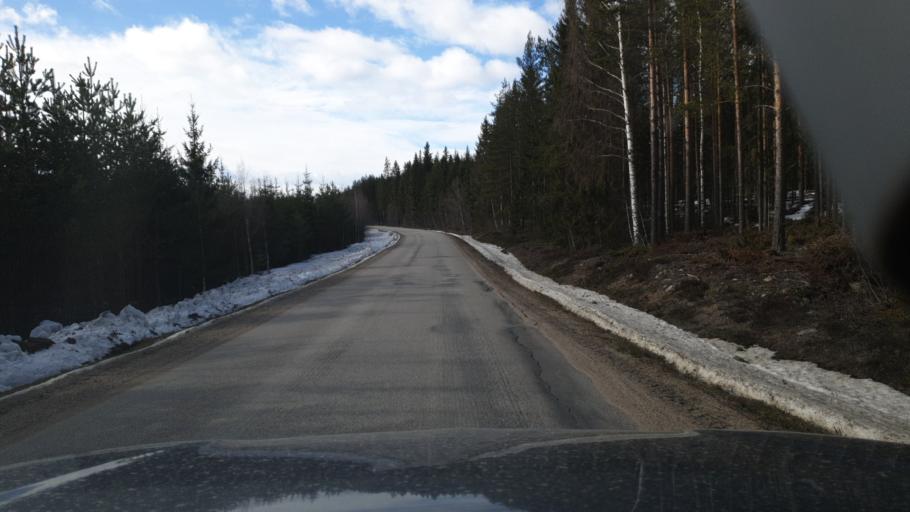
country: SE
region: Gaevleborg
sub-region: Ljusdals Kommun
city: Ljusdal
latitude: 61.8467
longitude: 15.9652
